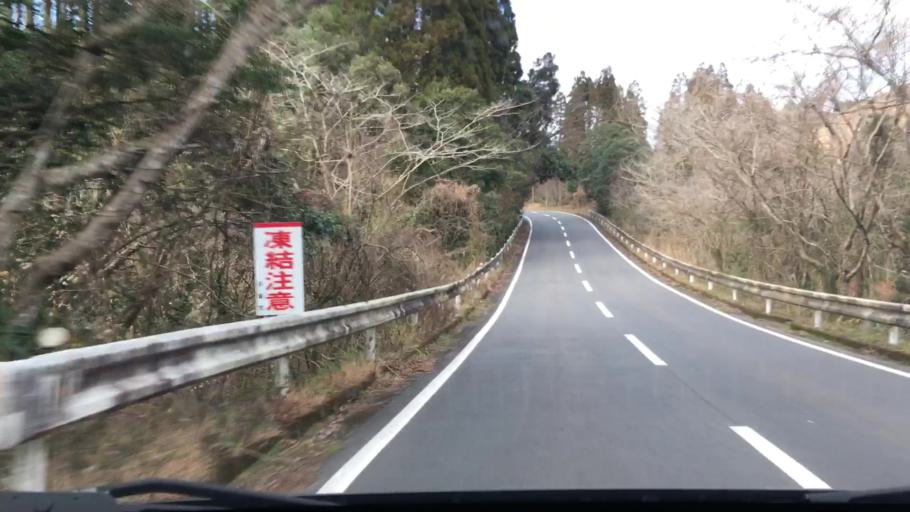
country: JP
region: Miyazaki
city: Nichinan
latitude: 31.7104
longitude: 131.3266
